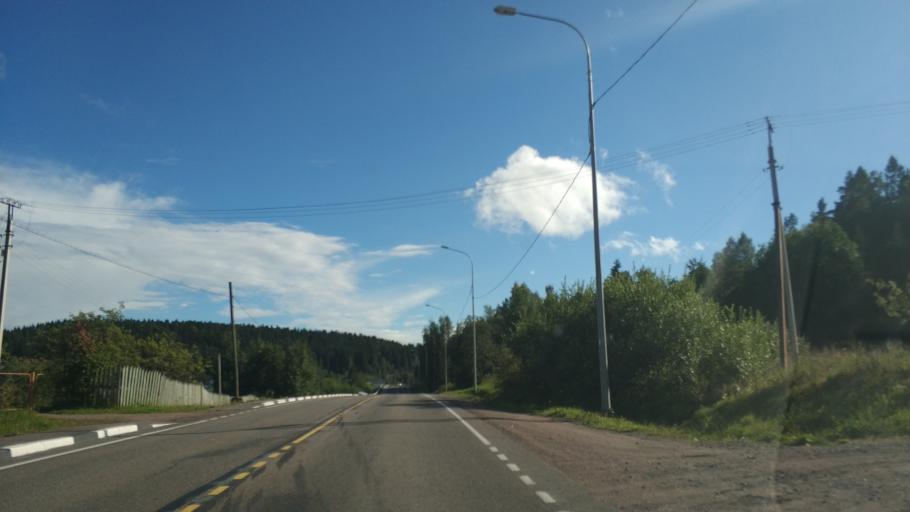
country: RU
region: Republic of Karelia
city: Sortavala
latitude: 61.6638
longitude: 30.6548
